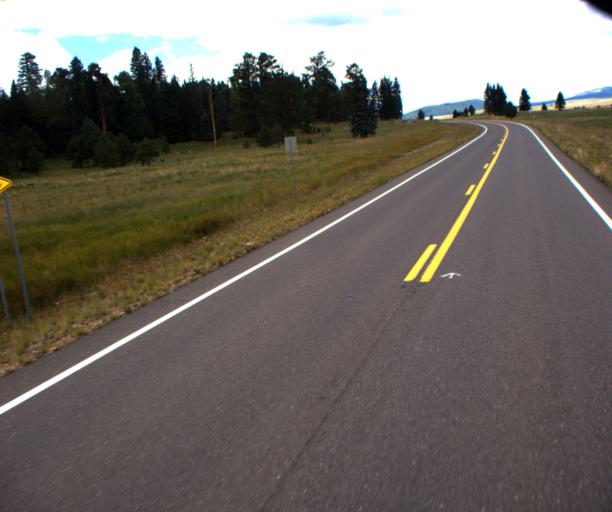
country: US
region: Arizona
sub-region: Apache County
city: Eagar
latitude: 33.9890
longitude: -109.5117
